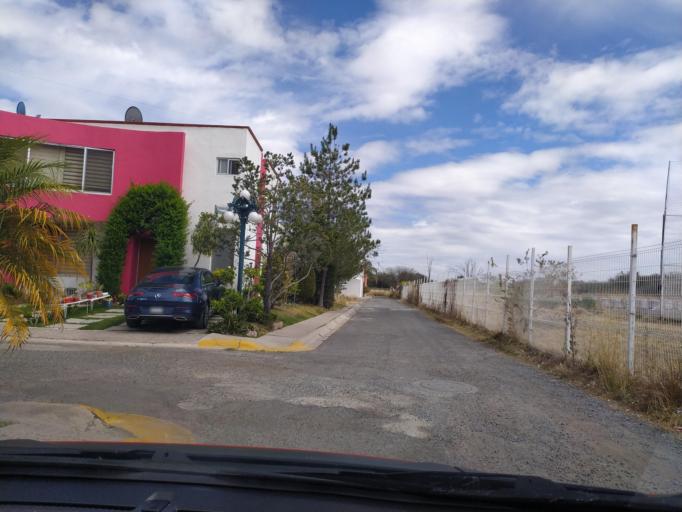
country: MX
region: Guanajuato
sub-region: Purisima del Rincon
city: Monte Grande
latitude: 21.0170
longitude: -101.8906
